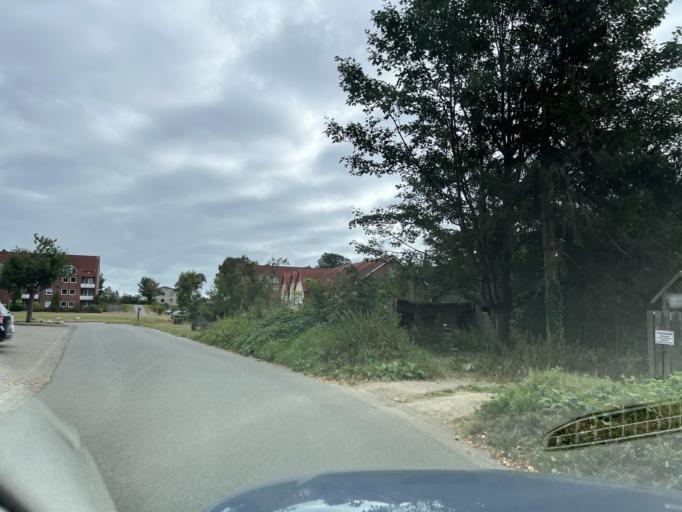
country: DE
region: Schleswig-Holstein
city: Heide
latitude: 54.1899
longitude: 9.0990
